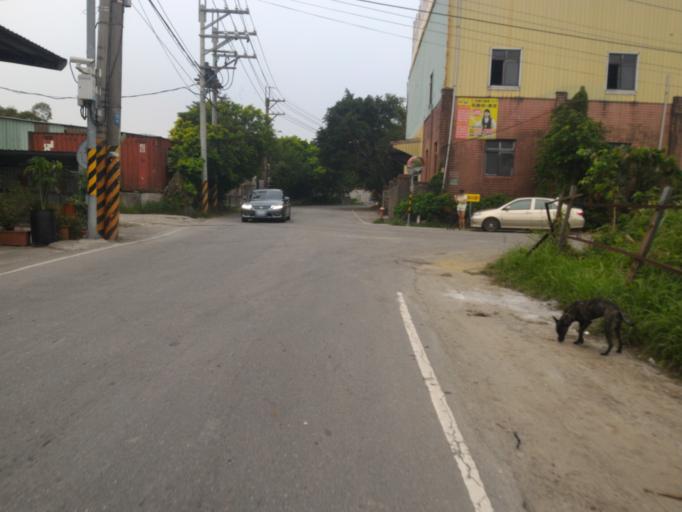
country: TW
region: Taipei
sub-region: Taipei
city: Banqiao
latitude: 24.9518
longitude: 121.4033
